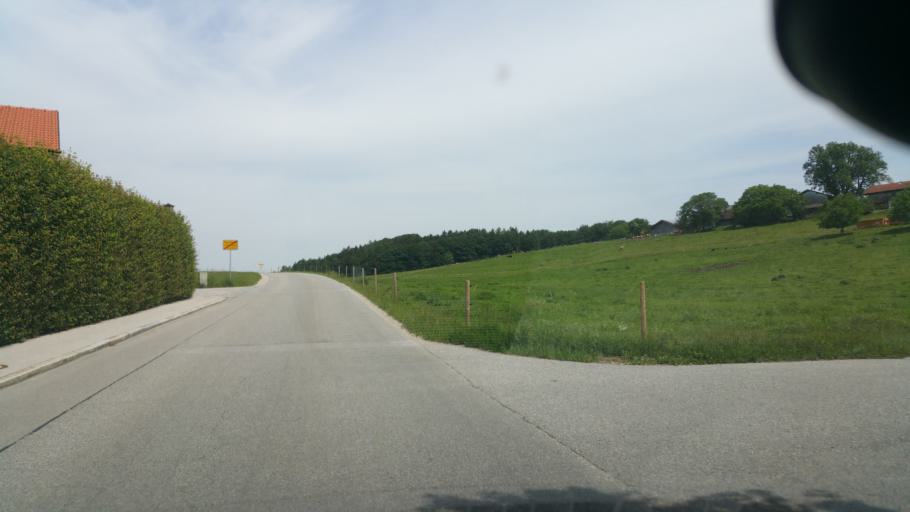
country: DE
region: Bavaria
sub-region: Upper Bavaria
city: Aschau im Chiemgau
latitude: 47.7935
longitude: 12.3259
